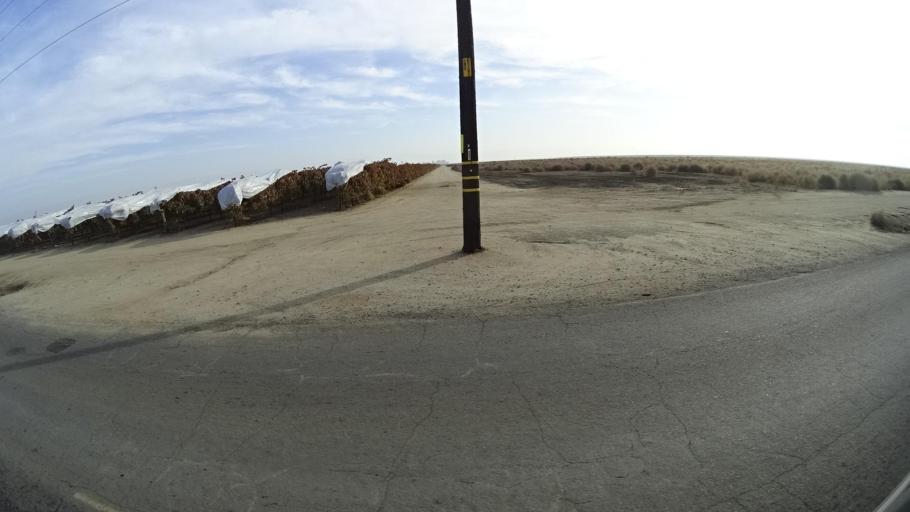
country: US
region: California
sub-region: Kern County
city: Delano
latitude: 35.7433
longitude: -119.2052
